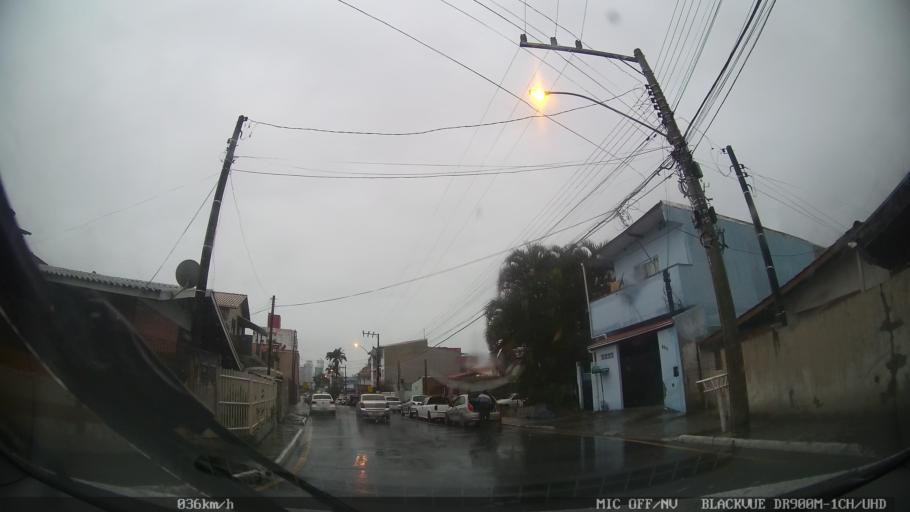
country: BR
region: Santa Catarina
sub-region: Balneario Camboriu
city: Balneario Camboriu
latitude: -27.0100
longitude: -48.6323
